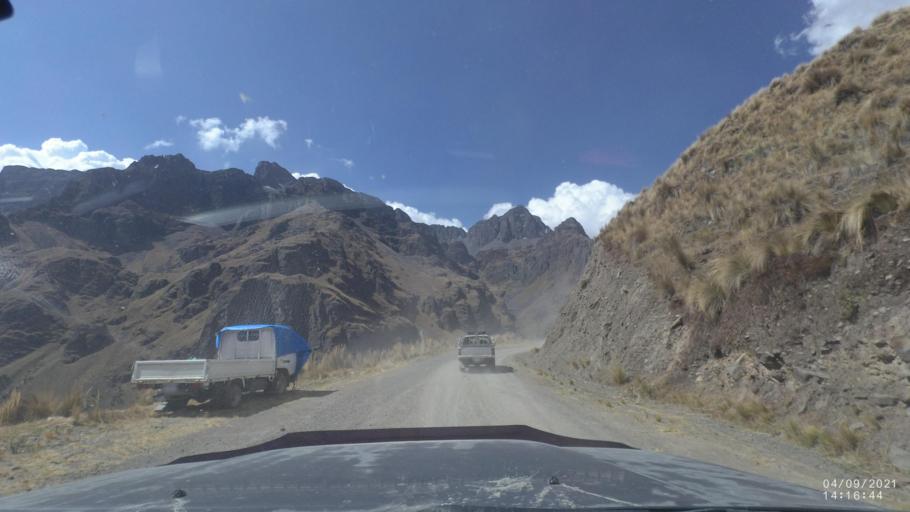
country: BO
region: Cochabamba
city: Sipe Sipe
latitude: -17.2310
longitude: -66.4377
